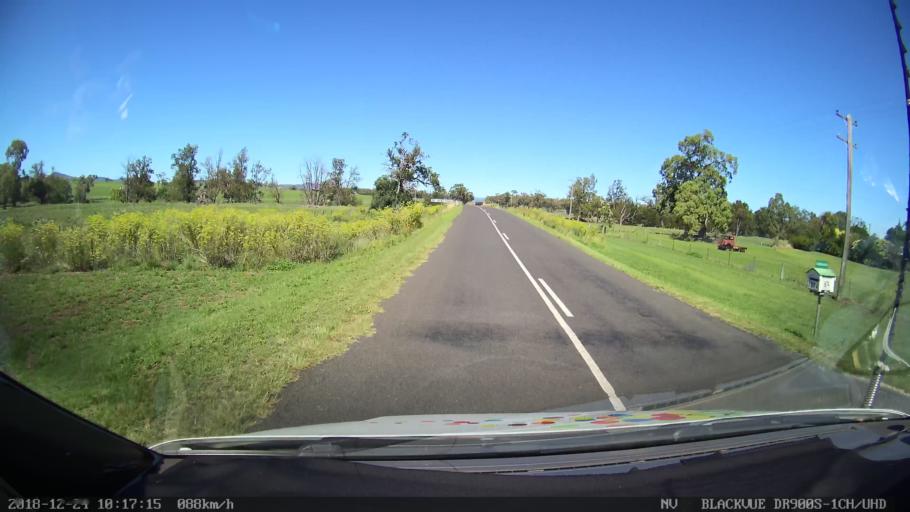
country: AU
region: New South Wales
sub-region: Liverpool Plains
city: Quirindi
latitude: -31.7193
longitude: 150.5939
